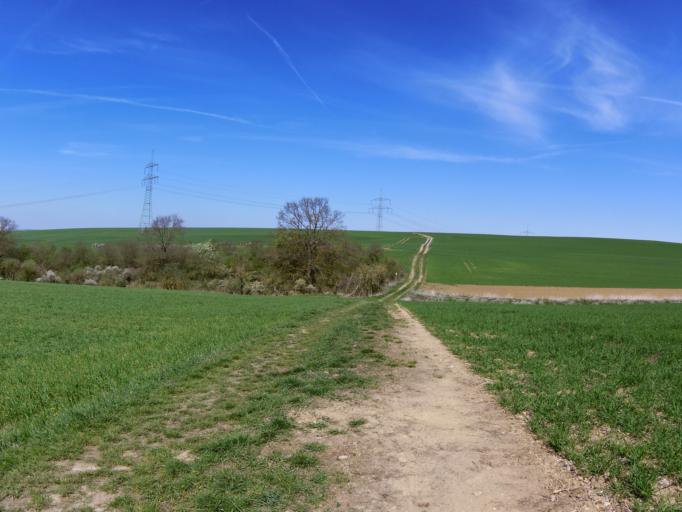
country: DE
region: Bavaria
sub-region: Regierungsbezirk Unterfranken
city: Rottendorf
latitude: 49.7833
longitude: 10.0533
